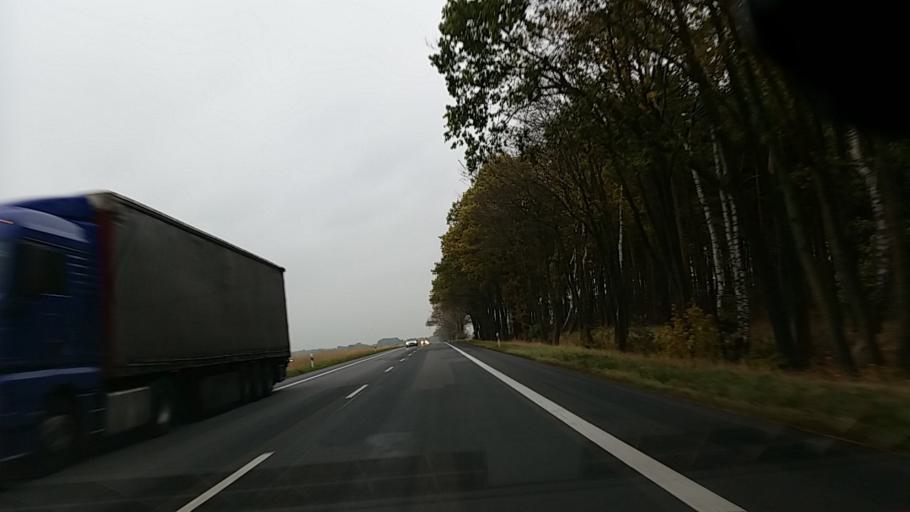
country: DE
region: Lower Saxony
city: Jelmstorf
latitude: 53.0866
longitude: 10.5280
